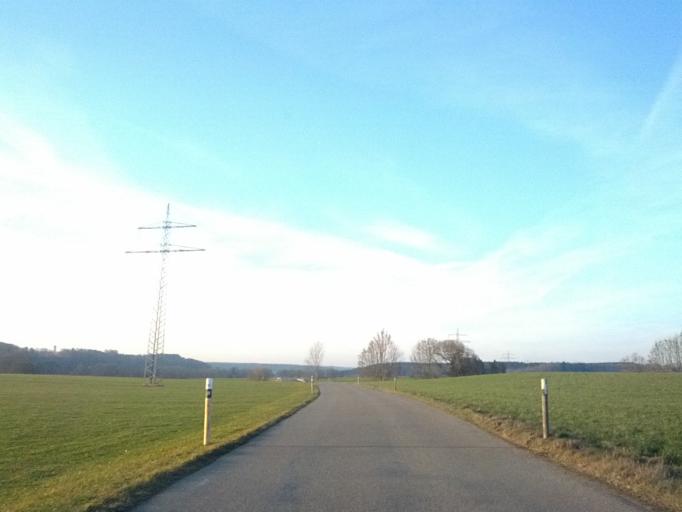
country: DE
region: Bavaria
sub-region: Swabia
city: Kronburg
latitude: 47.8809
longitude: 10.1697
